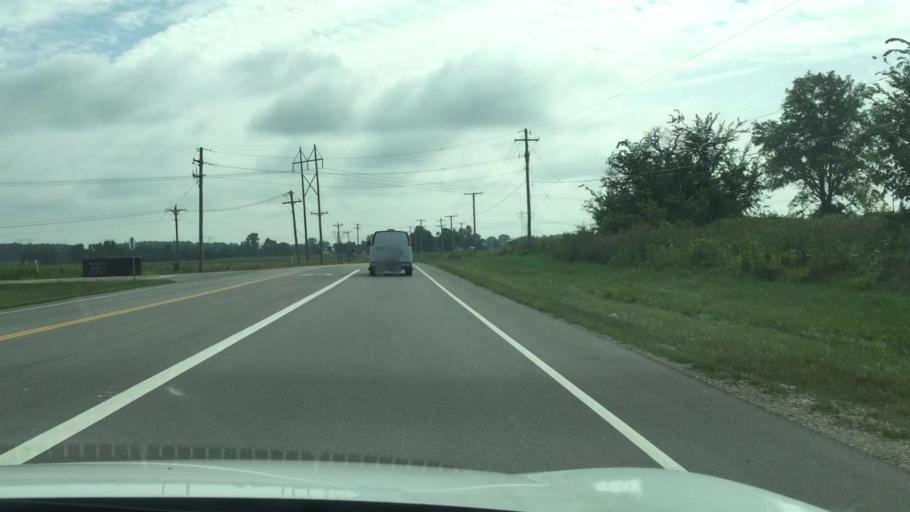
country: US
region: Ohio
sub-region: Union County
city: Marysville
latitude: 40.2046
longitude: -83.4038
